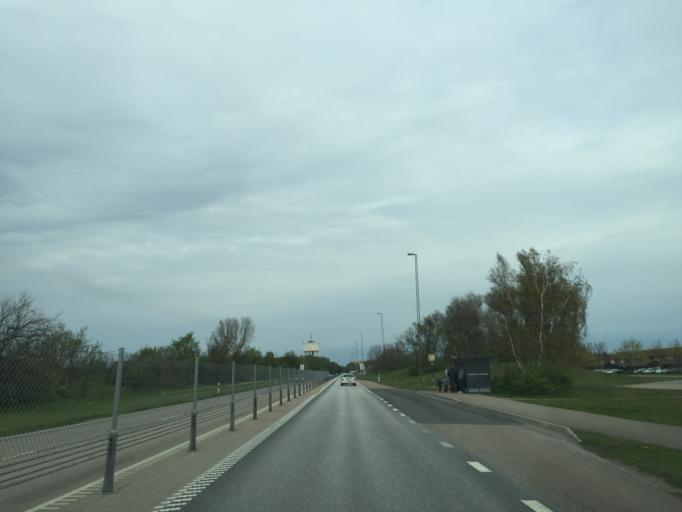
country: SE
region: Skane
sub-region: Hoganas Kommun
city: Hoganas
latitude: 56.1763
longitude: 12.5634
